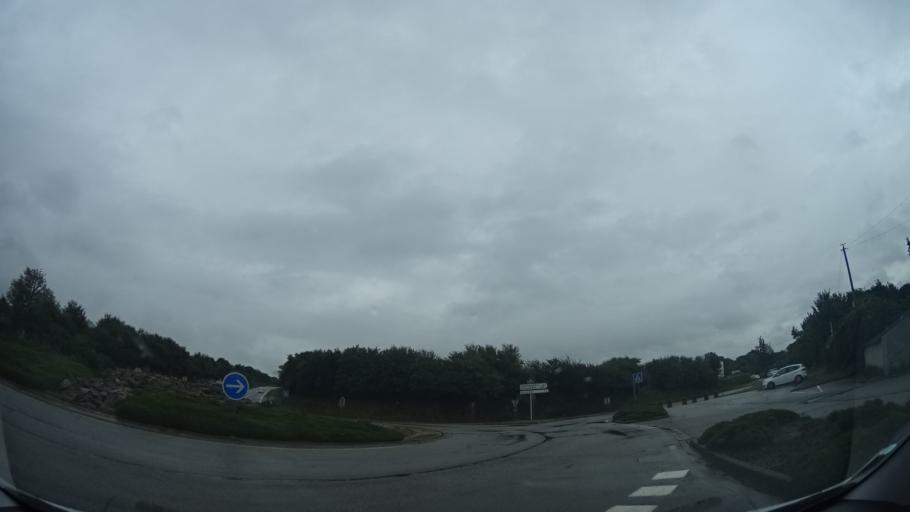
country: FR
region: Lower Normandy
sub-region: Departement de la Manche
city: Urville-Nacqueville
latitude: 49.6040
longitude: -1.7360
